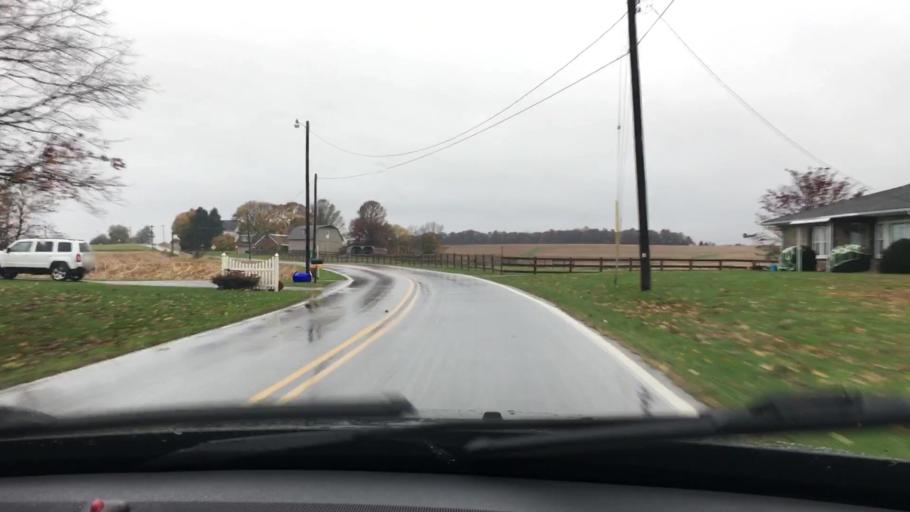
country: US
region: Pennsylvania
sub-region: York County
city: Susquehanna Trails
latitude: 39.8085
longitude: -76.4078
